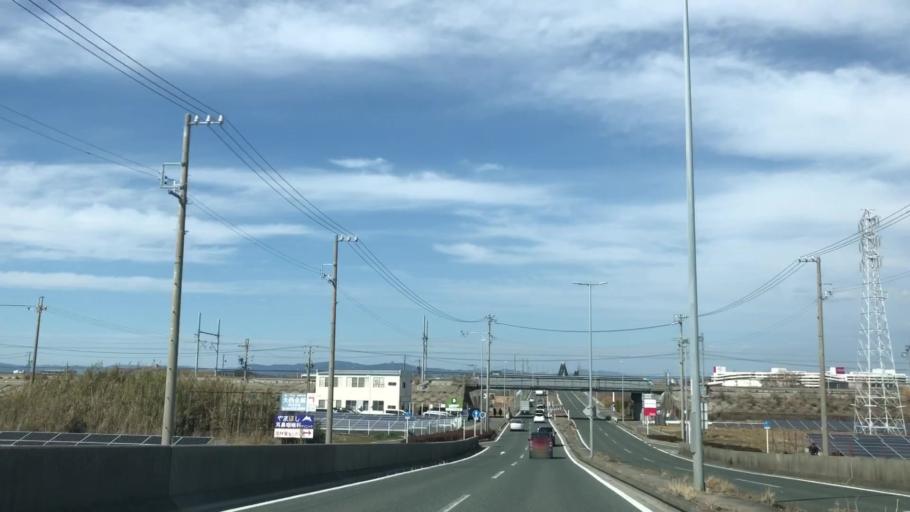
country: JP
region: Shizuoka
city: Hamamatsu
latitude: 34.6864
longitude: 137.6476
